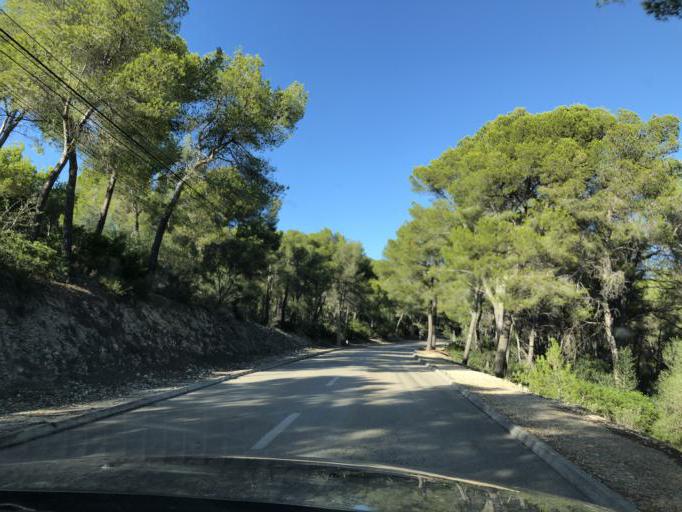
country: ES
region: Balearic Islands
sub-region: Illes Balears
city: Camp de Mar
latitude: 39.5400
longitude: 2.4054
